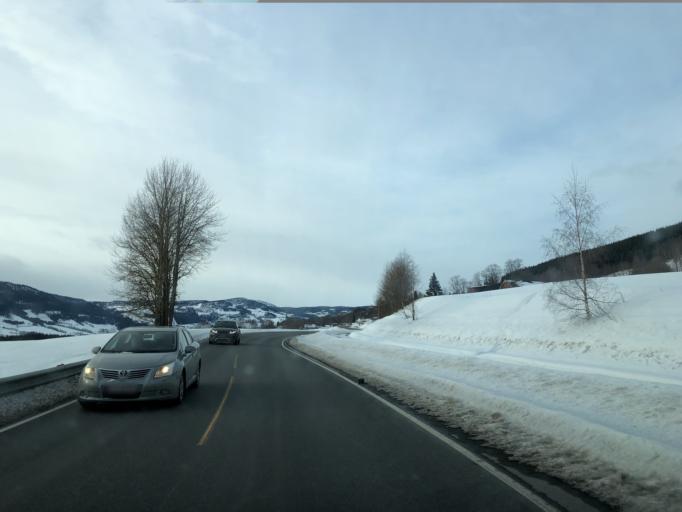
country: NO
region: Oppland
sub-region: Gausdal
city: Segalstad bru
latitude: 61.2415
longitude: 10.1988
